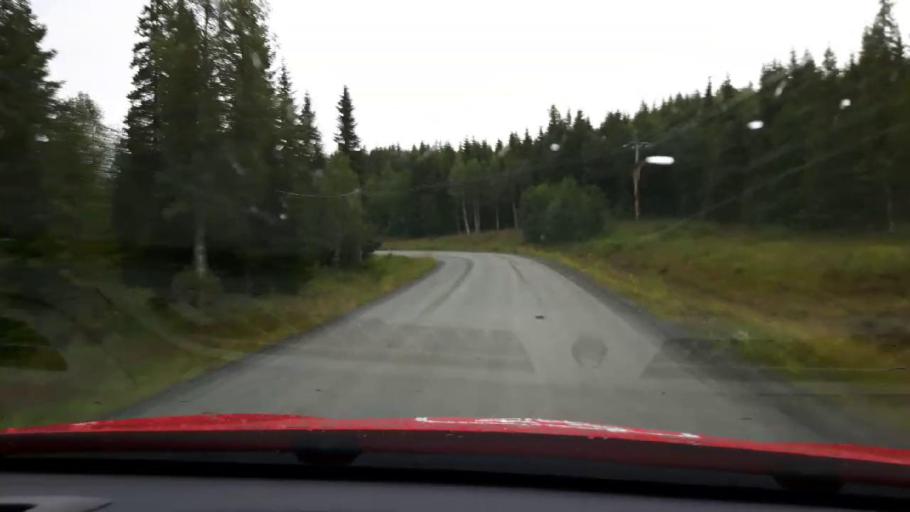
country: SE
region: Jaemtland
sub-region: Are Kommun
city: Are
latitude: 63.4081
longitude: 12.8324
